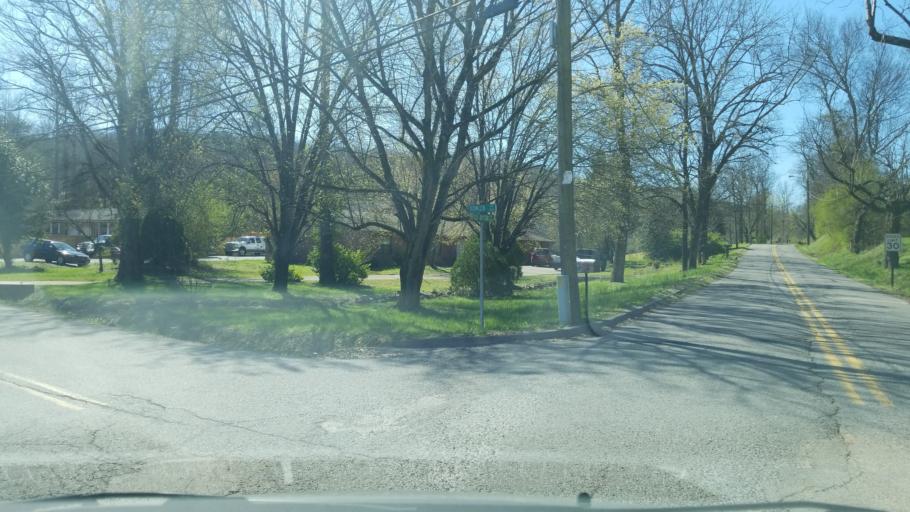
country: US
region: Tennessee
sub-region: Hamilton County
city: Falling Water
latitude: 35.1713
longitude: -85.2584
